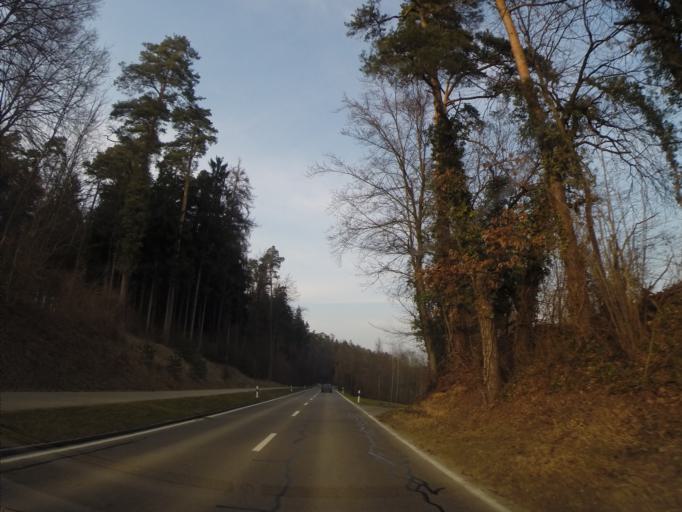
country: CH
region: Zurich
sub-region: Bezirk Andelfingen
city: Henggart
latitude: 47.5481
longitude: 8.6831
